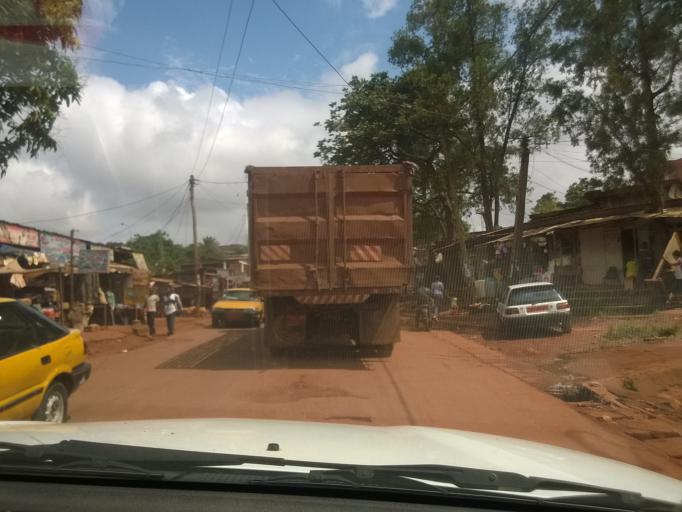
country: CM
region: Centre
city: Yaounde
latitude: 3.8718
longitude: 11.5411
